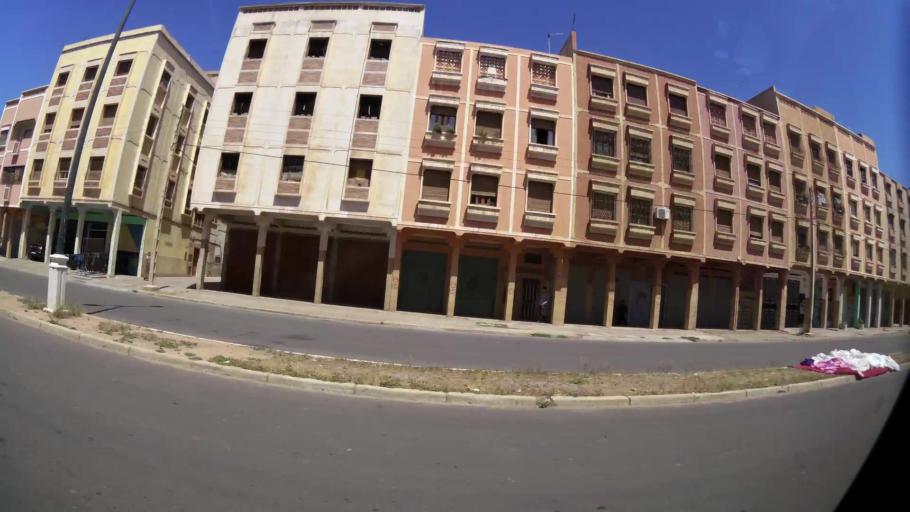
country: MA
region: Souss-Massa-Draa
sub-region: Inezgane-Ait Mellou
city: Inezgane
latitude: 30.3380
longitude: -9.5013
